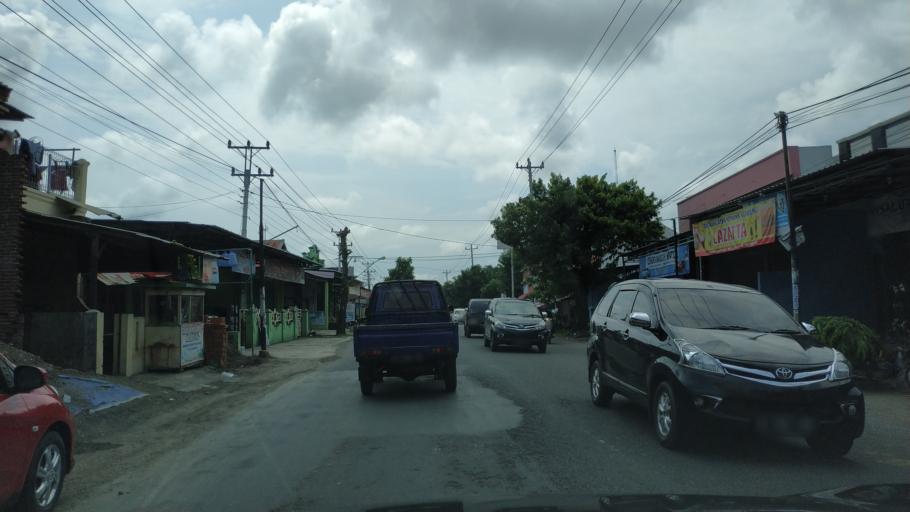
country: ID
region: Central Java
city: Tegal
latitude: -6.9015
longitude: 109.1257
